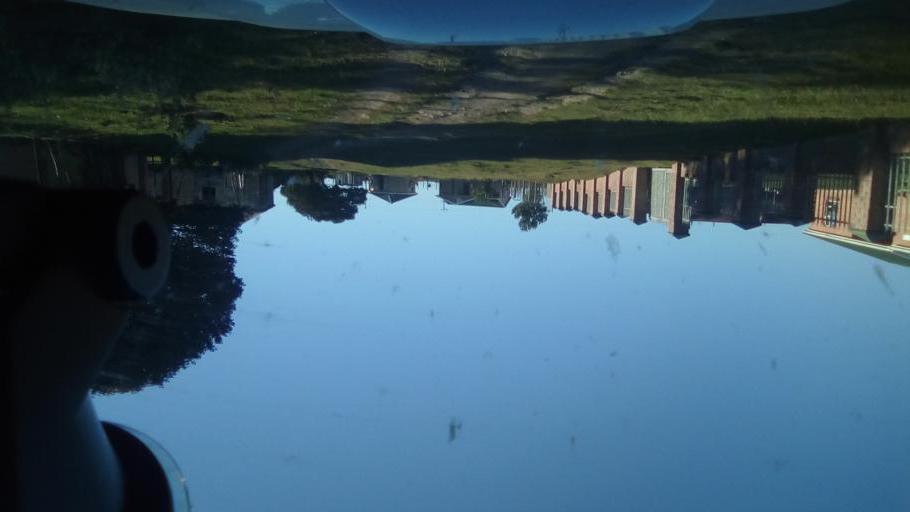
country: ZA
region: Eastern Cape
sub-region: Buffalo City Metropolitan Municipality
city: Bhisho
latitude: -32.9520
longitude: 27.2940
